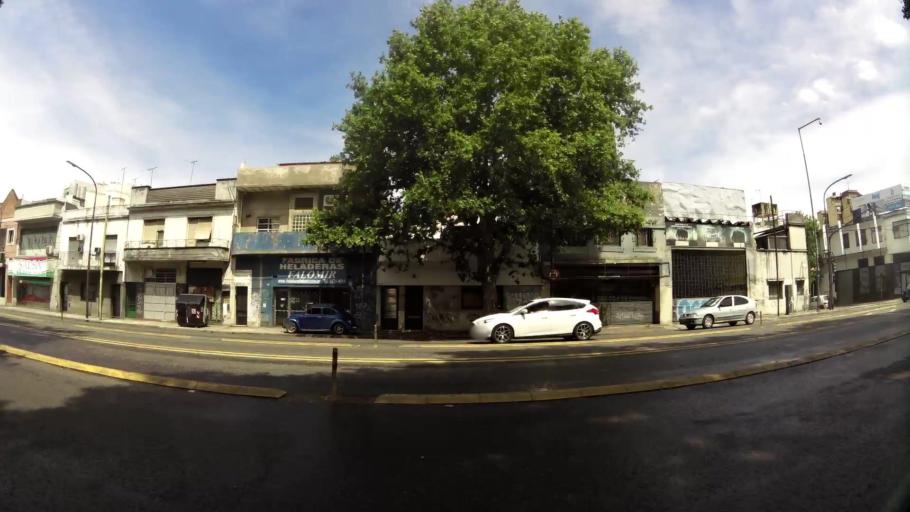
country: AR
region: Buenos Aires F.D.
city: Villa Santa Rita
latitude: -34.6238
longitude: -58.4832
